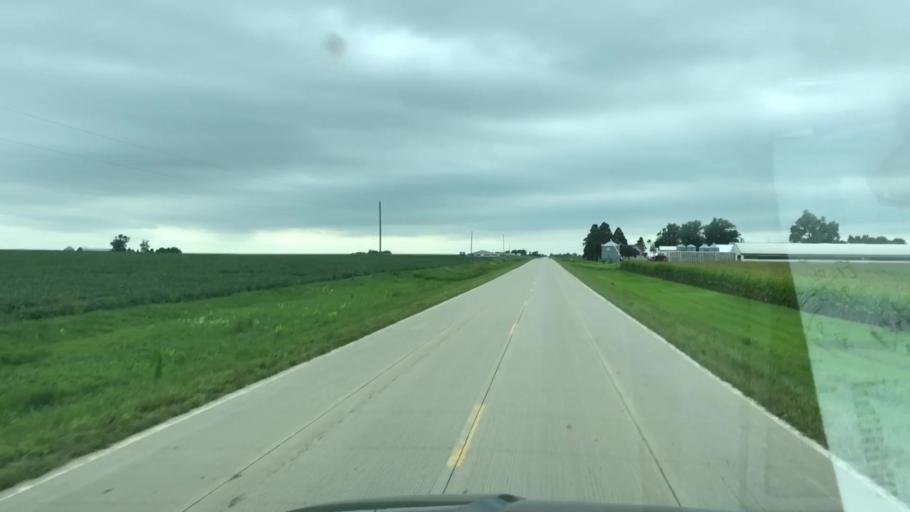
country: US
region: Iowa
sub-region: O'Brien County
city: Sheldon
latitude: 43.1352
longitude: -95.9793
